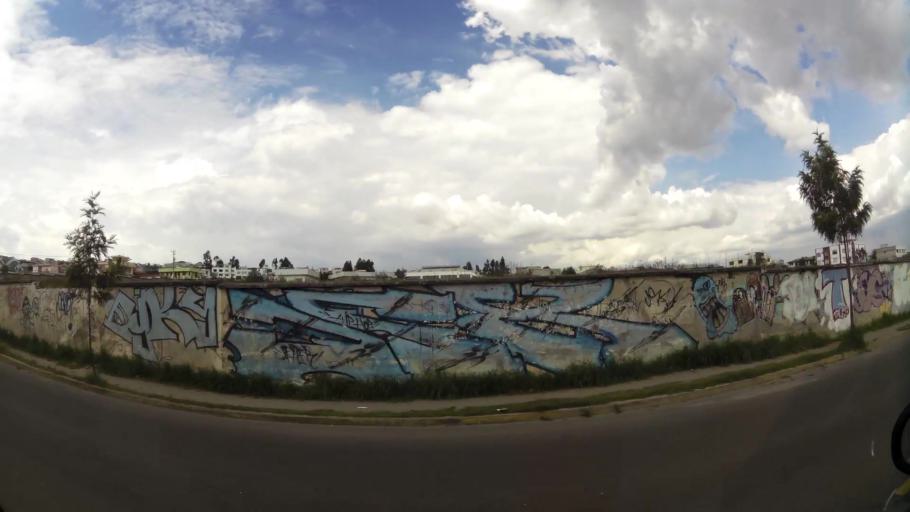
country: EC
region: Pichincha
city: Quito
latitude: -0.0935
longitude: -78.4430
